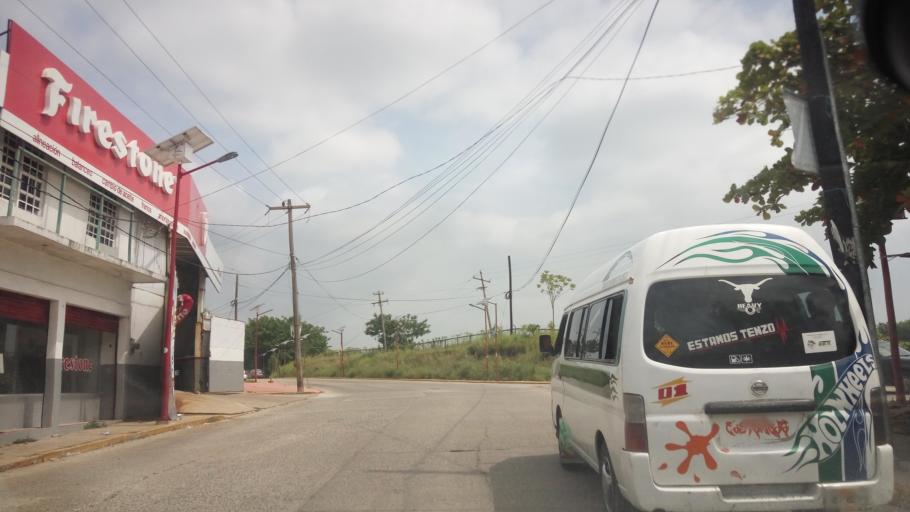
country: MX
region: Chiapas
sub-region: Reforma
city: El Carmen (El Limon)
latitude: 17.8708
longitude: -93.1491
